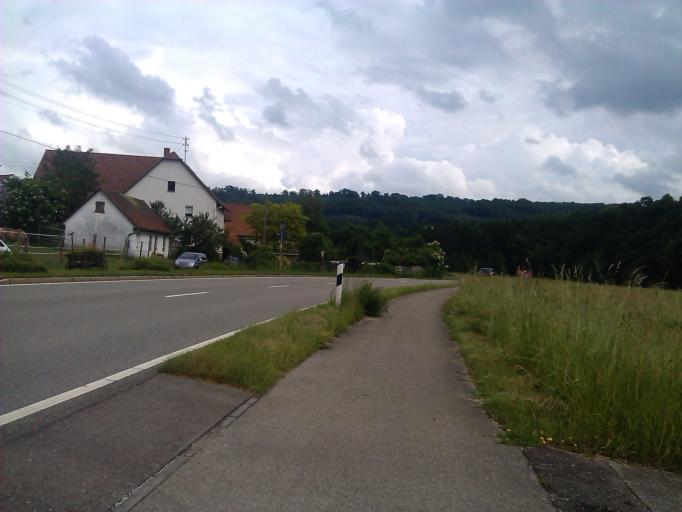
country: DE
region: Baden-Wuerttemberg
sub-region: Regierungsbezirk Stuttgart
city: Obergroningen
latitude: 48.9095
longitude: 9.9475
